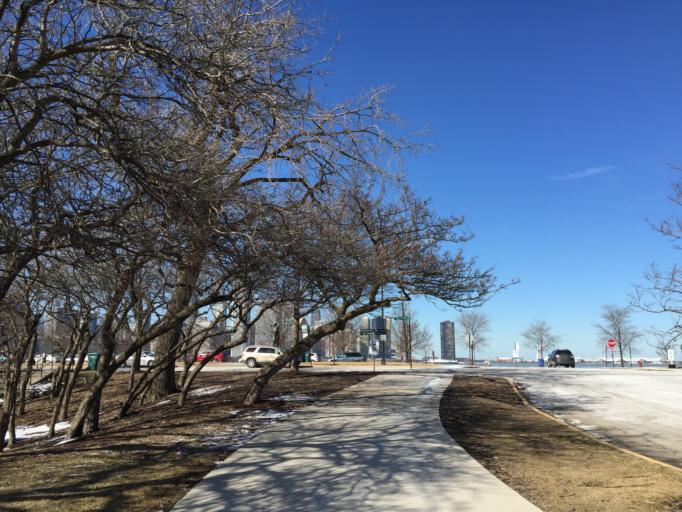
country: US
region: Illinois
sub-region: Cook County
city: Chicago
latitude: 41.8658
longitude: -87.6102
